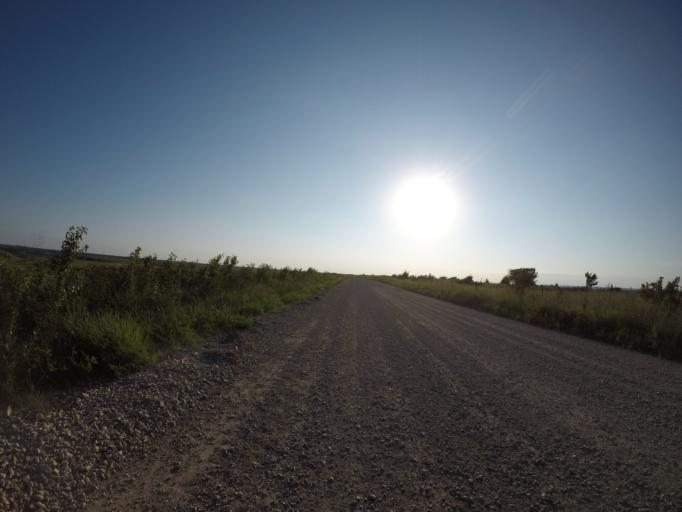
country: US
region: Kansas
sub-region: Riley County
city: Ogden
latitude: 39.0488
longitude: -96.6876
